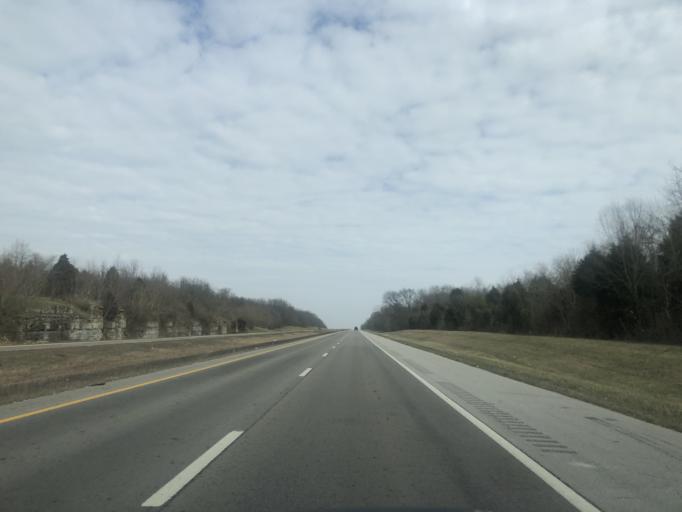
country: US
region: Tennessee
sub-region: Maury County
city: Mount Pleasant
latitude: 35.5742
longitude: -87.1554
